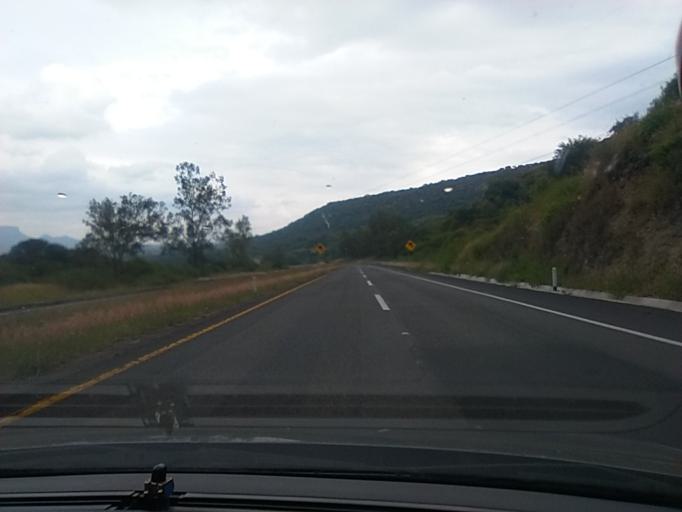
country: MX
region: Jalisco
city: Ocotlan
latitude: 20.4236
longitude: -102.7697
